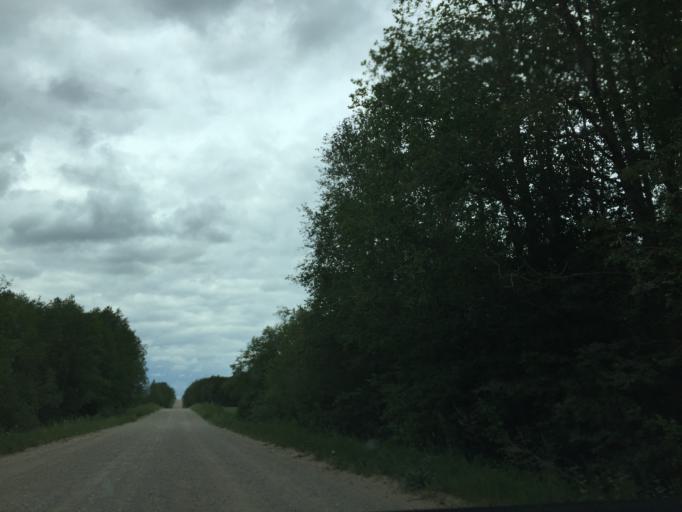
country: LV
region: Dagda
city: Dagda
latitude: 55.9983
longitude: 27.6092
